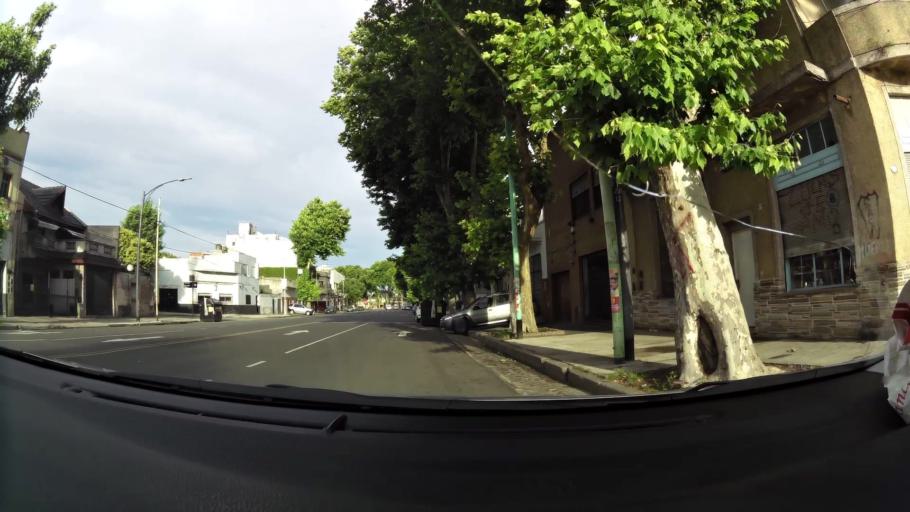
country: AR
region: Buenos Aires F.D.
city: Villa Lugano
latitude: -34.6450
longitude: -58.4275
